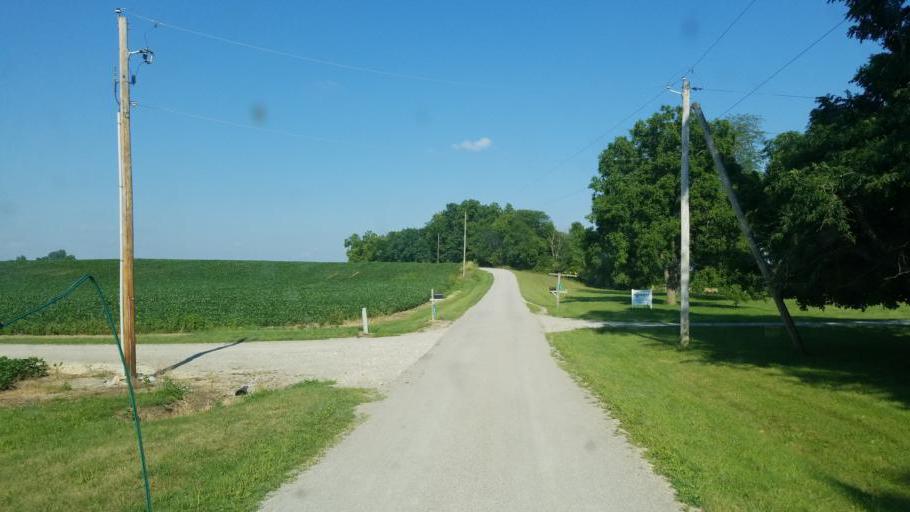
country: US
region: Ohio
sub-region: Wyandot County
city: Upper Sandusky
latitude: 40.7886
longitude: -83.3384
